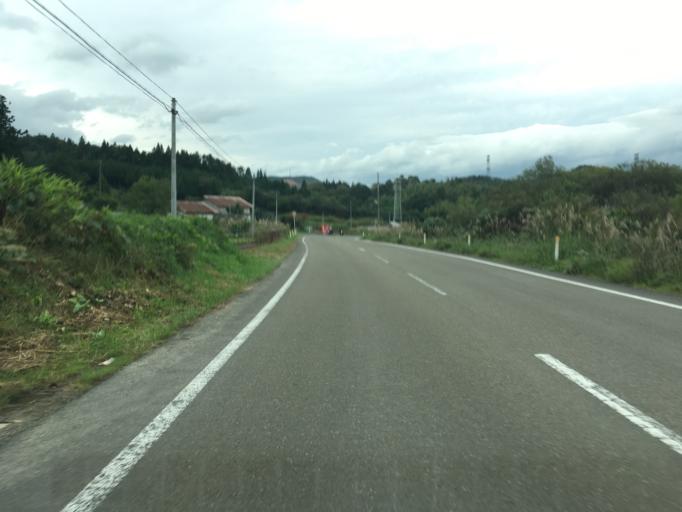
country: JP
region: Miyagi
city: Marumori
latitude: 37.8847
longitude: 140.7121
